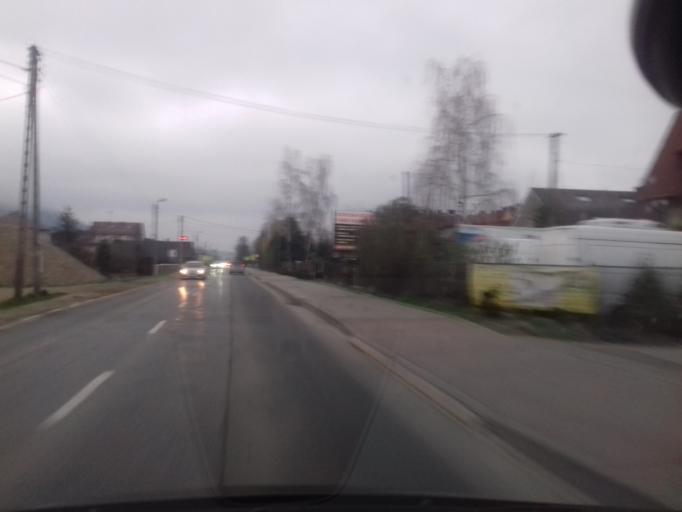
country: PL
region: Lesser Poland Voivodeship
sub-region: Powiat limanowski
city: Mszana Dolna
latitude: 49.6769
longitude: 20.0628
